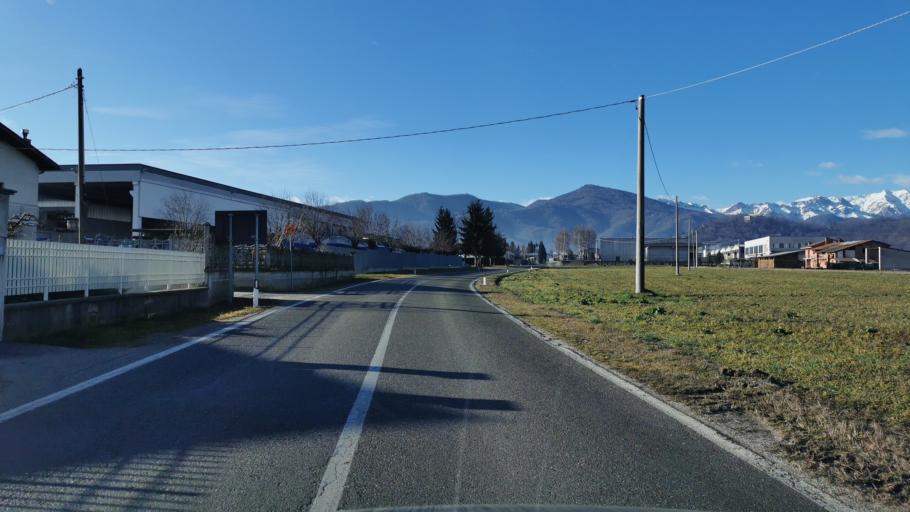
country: IT
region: Piedmont
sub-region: Provincia di Cuneo
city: Caraglio
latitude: 44.4273
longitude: 7.4449
